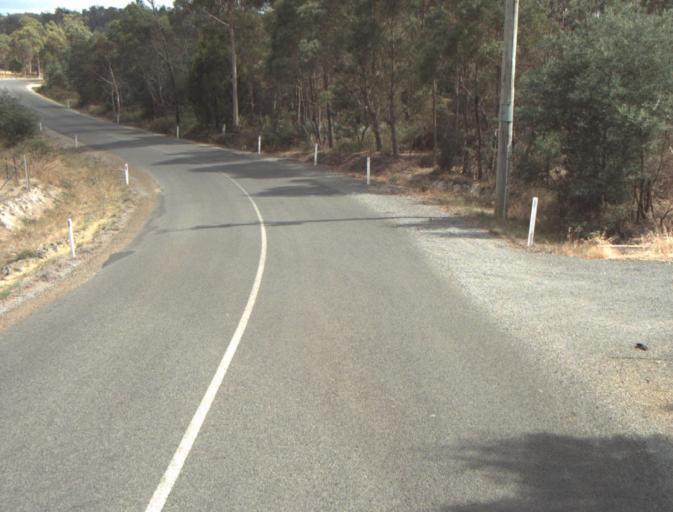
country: AU
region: Tasmania
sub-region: Launceston
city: Mayfield
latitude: -41.2111
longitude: 147.1336
